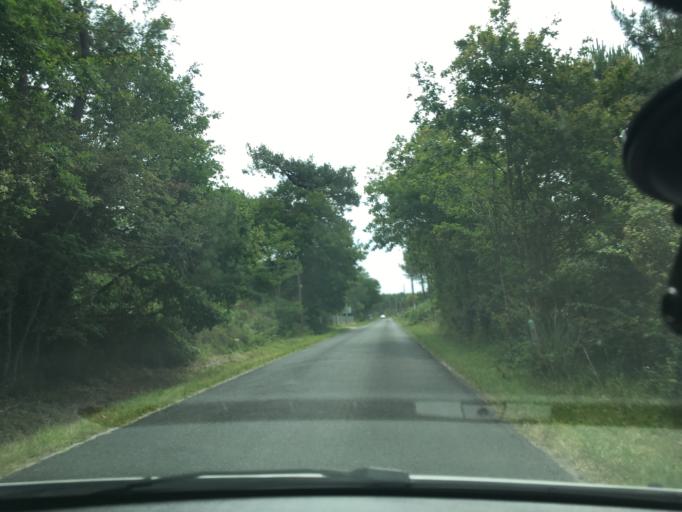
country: FR
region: Aquitaine
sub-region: Departement de la Gironde
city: Gaillan-en-Medoc
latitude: 45.3540
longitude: -1.0530
